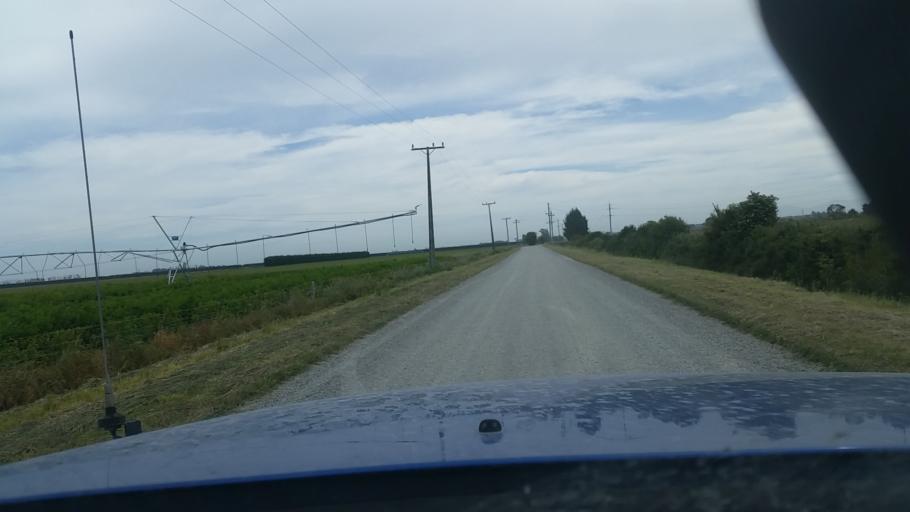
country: NZ
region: Canterbury
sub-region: Ashburton District
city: Tinwald
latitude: -44.0066
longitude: 171.7740
